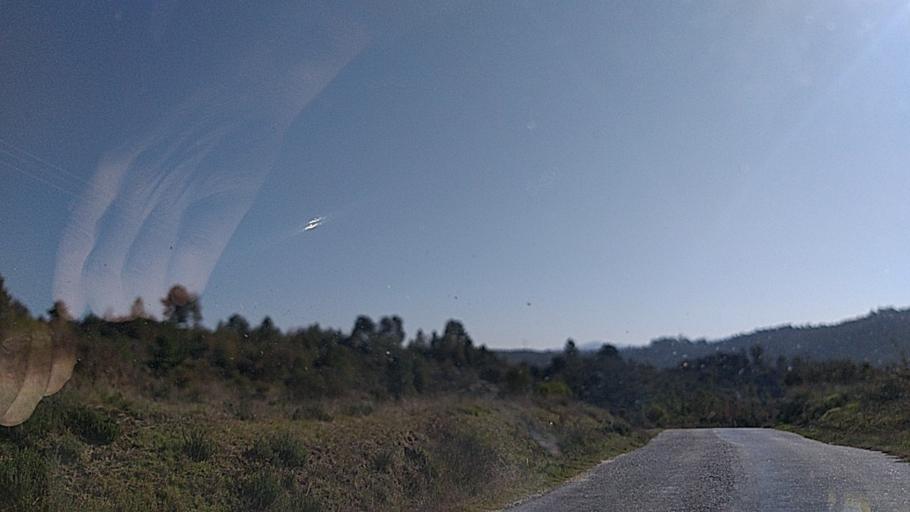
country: PT
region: Guarda
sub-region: Celorico da Beira
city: Celorico da Beira
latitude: 40.6855
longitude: -7.4152
